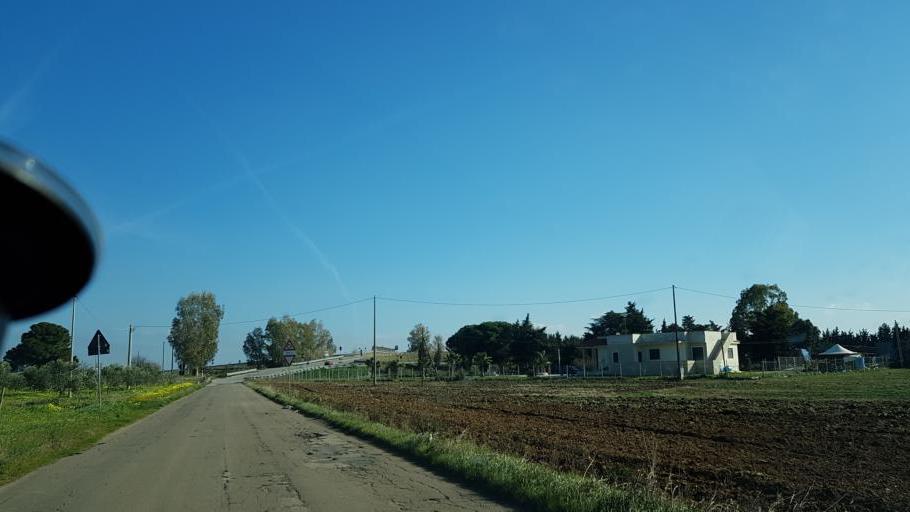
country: IT
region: Apulia
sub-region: Provincia di Brindisi
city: Brindisi
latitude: 40.6063
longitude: 17.8800
